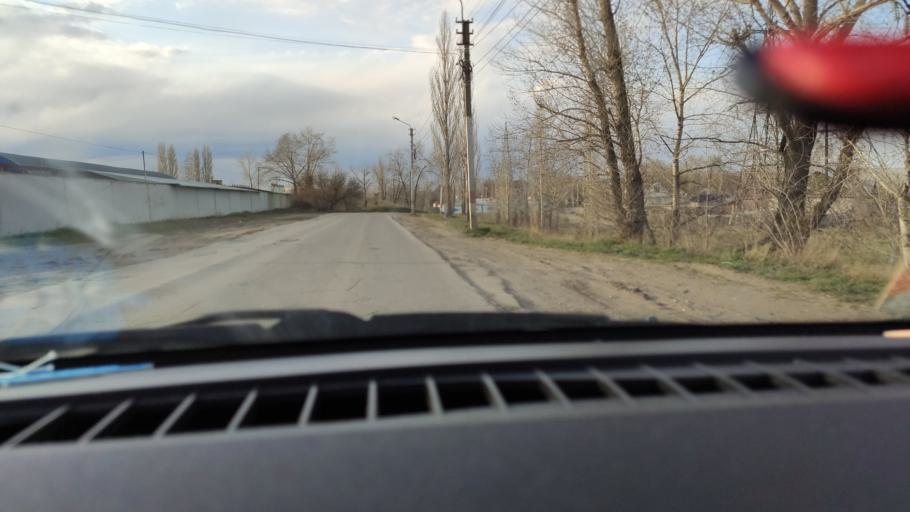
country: RU
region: Saratov
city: Engel's
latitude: 51.4916
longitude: 46.0520
